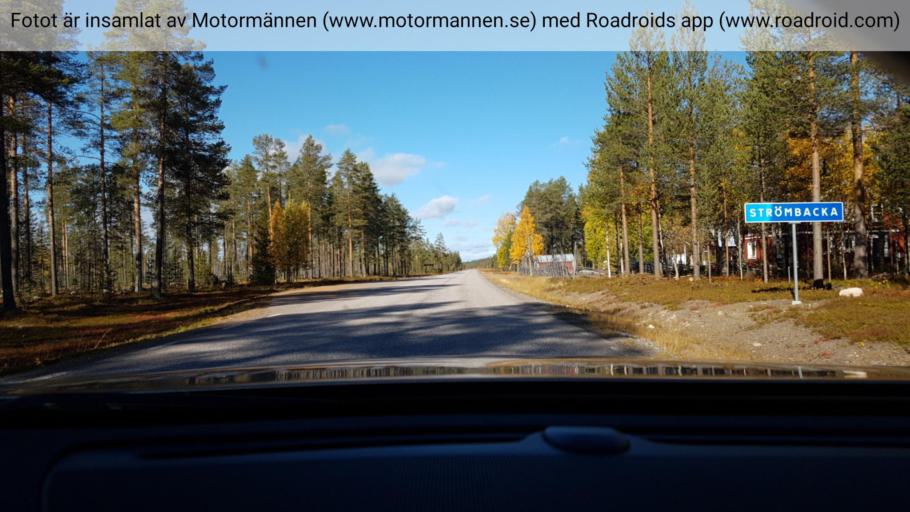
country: SE
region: Norrbotten
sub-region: Arvidsjaurs Kommun
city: Arvidsjaur
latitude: 65.6872
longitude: 18.7903
